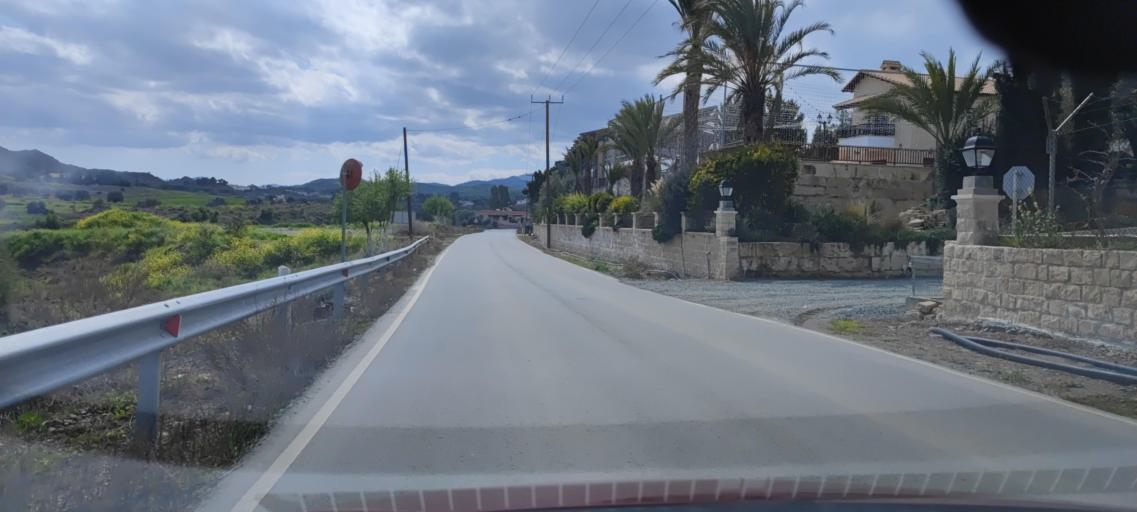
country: CY
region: Lefkosia
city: Pera
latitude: 35.0178
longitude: 33.2970
